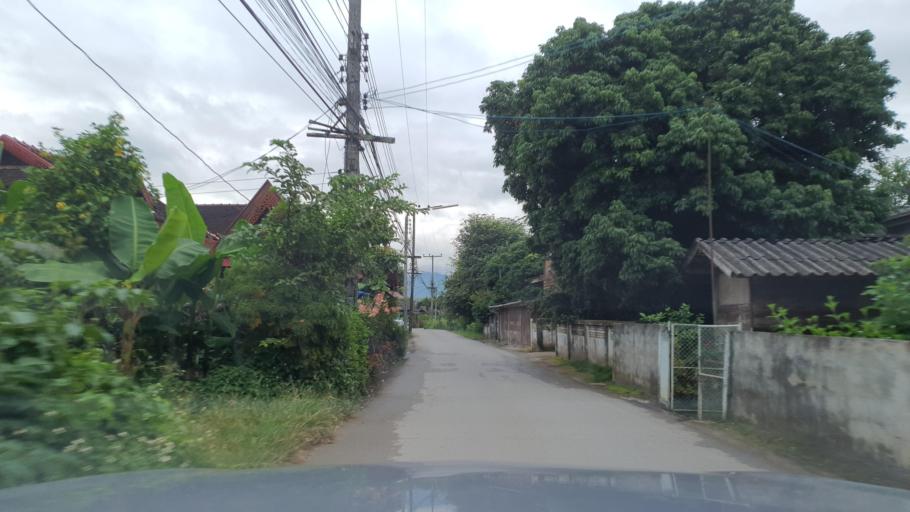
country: TH
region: Chiang Mai
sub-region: Amphoe Chiang Dao
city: Chiang Dao
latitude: 19.3301
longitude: 98.9506
